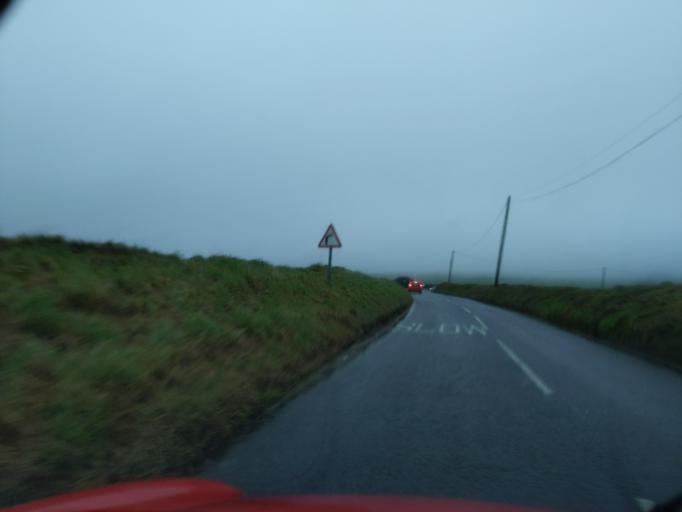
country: GB
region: England
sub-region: Cornwall
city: Camelford
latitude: 50.6428
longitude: -4.6963
